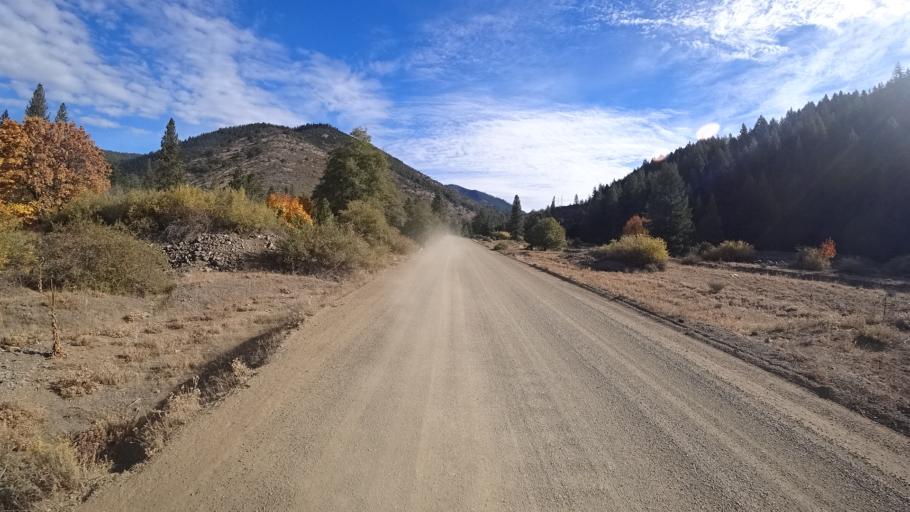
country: US
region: California
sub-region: Siskiyou County
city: Yreka
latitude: 41.7128
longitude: -122.8049
